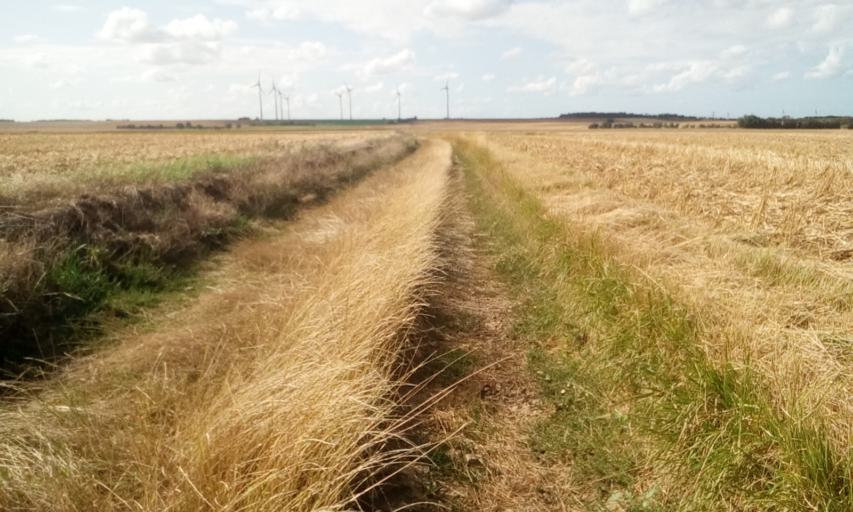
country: FR
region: Lower Normandy
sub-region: Departement du Calvados
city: Saint-Sylvain
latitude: 49.0790
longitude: -0.2370
